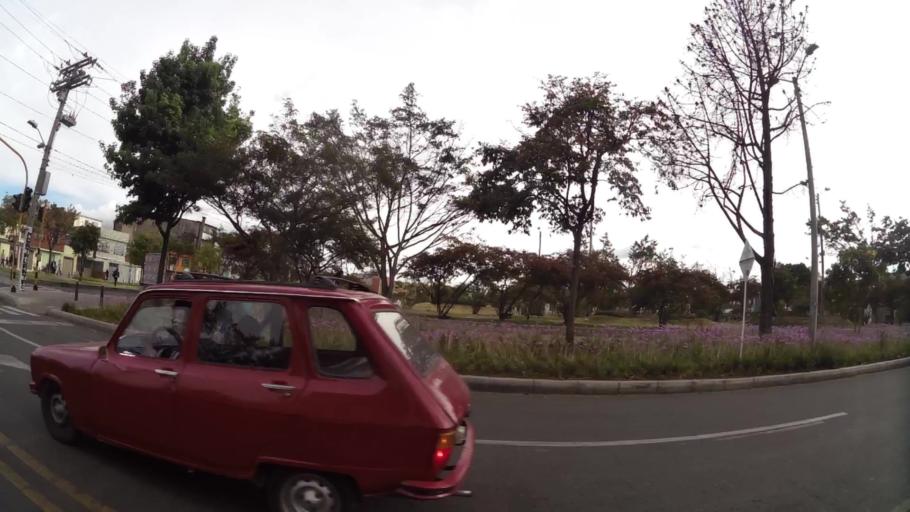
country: CO
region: Cundinamarca
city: Soacha
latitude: 4.6199
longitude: -74.1569
